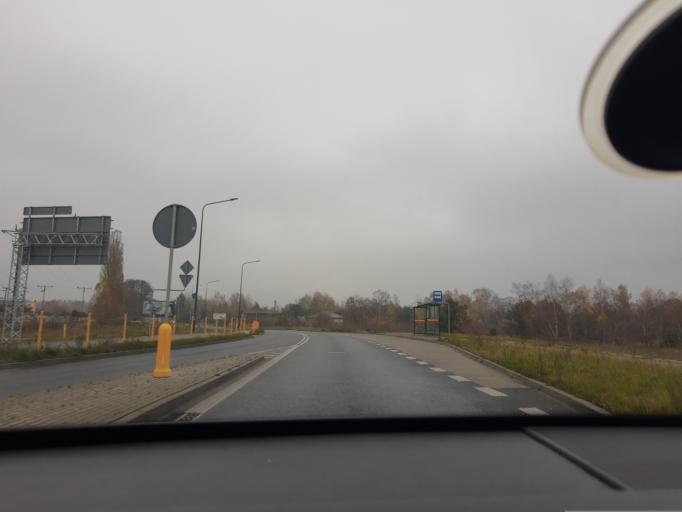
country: PL
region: Lodz Voivodeship
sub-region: Powiat pabianicki
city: Konstantynow Lodzki
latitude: 51.7306
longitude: 19.3590
